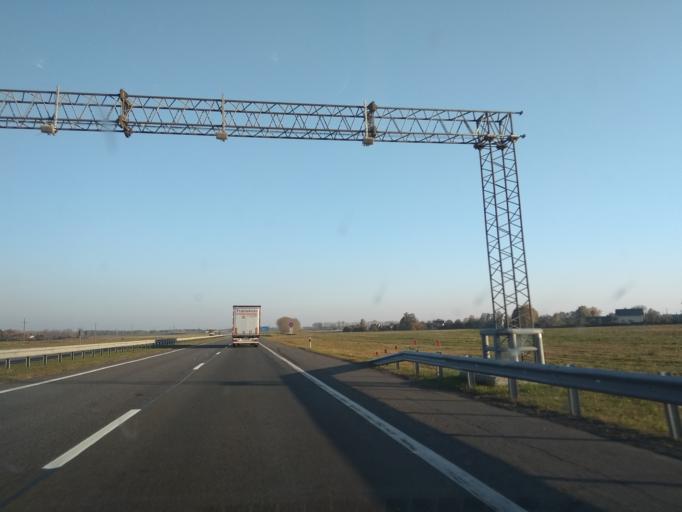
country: BY
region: Brest
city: Kobryn
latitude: 52.1921
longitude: 24.3084
